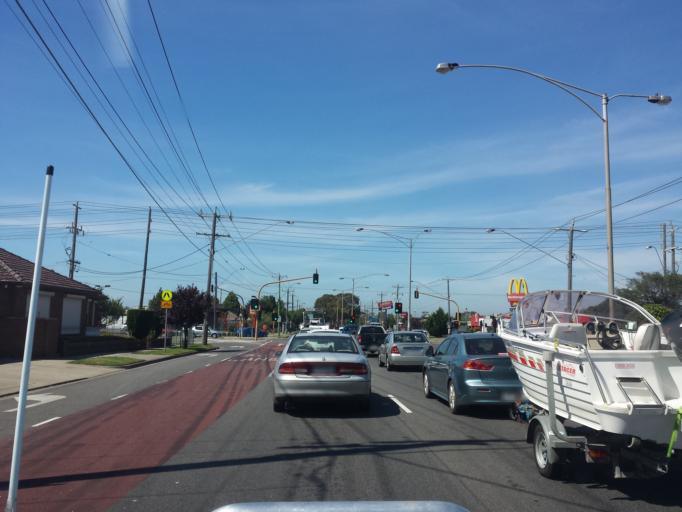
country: AU
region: Victoria
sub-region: Hobsons Bay
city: Altona North
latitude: -37.8306
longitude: 144.8485
